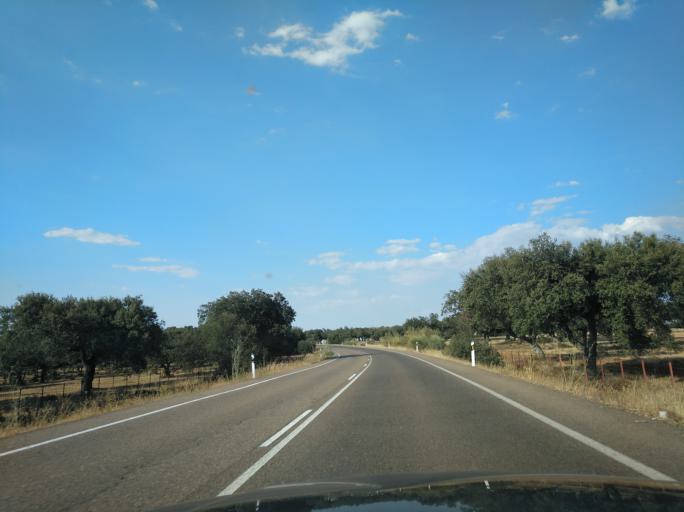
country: ES
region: Extremadura
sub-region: Provincia de Badajoz
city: Villanueva del Fresno
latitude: 38.3961
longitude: -7.1447
